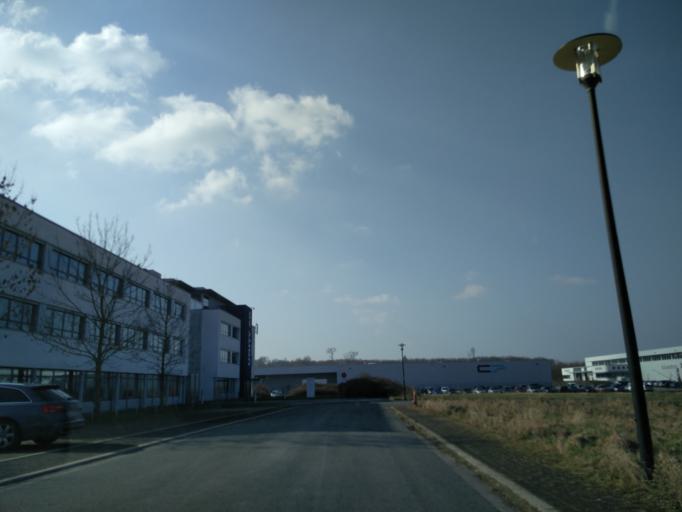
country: DE
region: North Rhine-Westphalia
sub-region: Regierungsbezirk Detmold
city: Salzkotten
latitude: 51.6068
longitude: 8.6116
